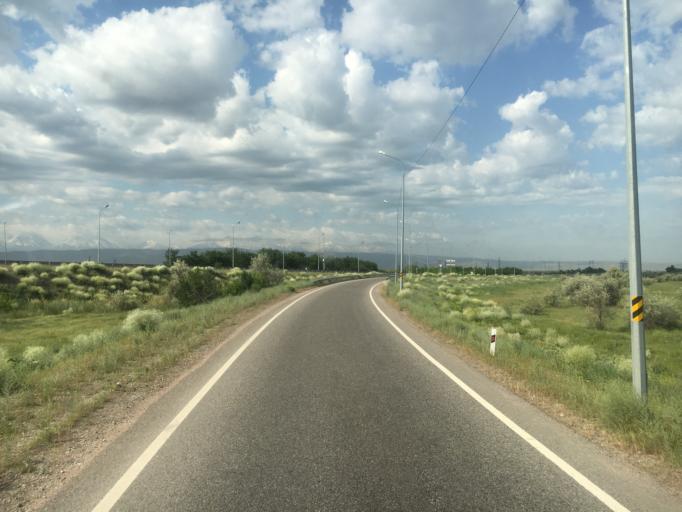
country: KZ
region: Zhambyl
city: Taraz
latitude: 42.8227
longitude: 71.1613
